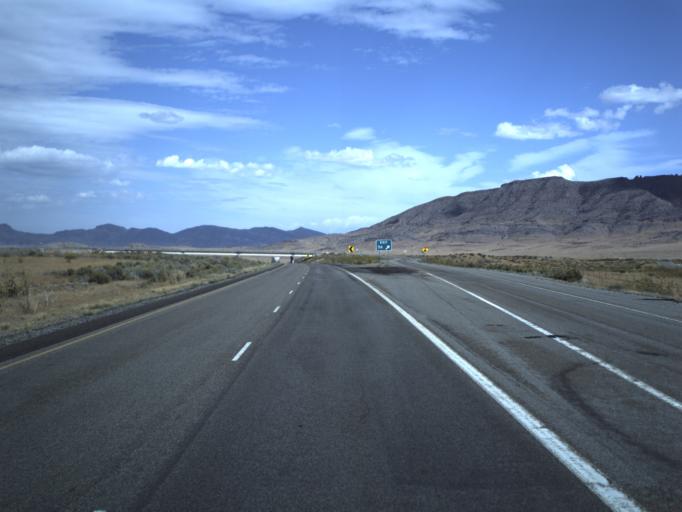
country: US
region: Utah
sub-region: Tooele County
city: Grantsville
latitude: 40.7660
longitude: -112.9893
